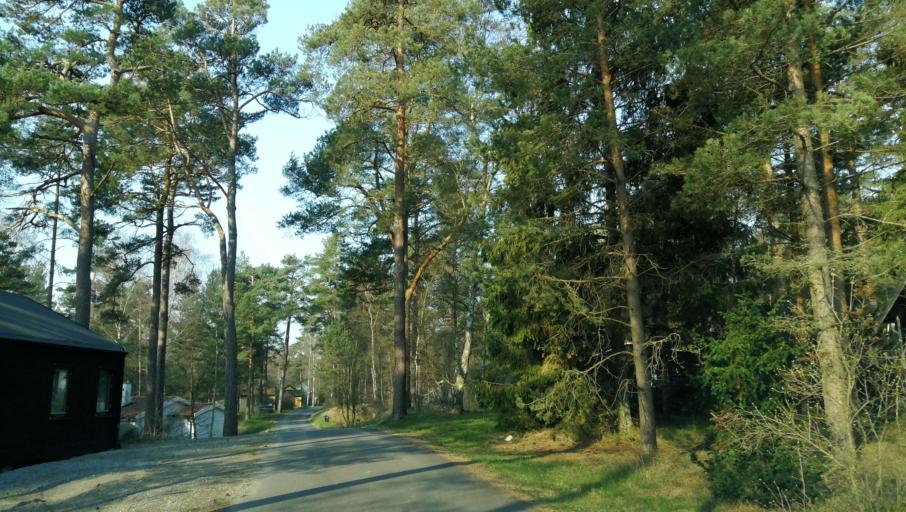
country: SE
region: Skane
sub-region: Ystads Kommun
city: Kopingebro
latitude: 55.4367
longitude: 13.8856
